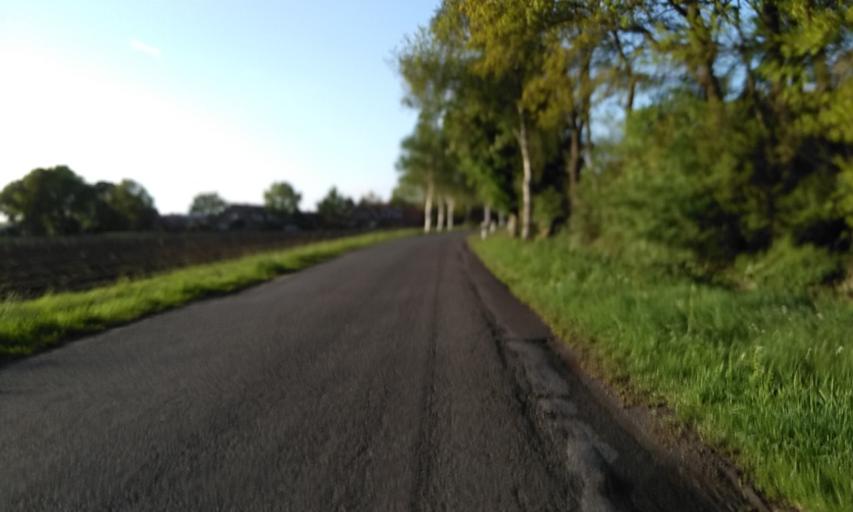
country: DE
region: Lower Saxony
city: Harsefeld
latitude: 53.4024
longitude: 9.5049
